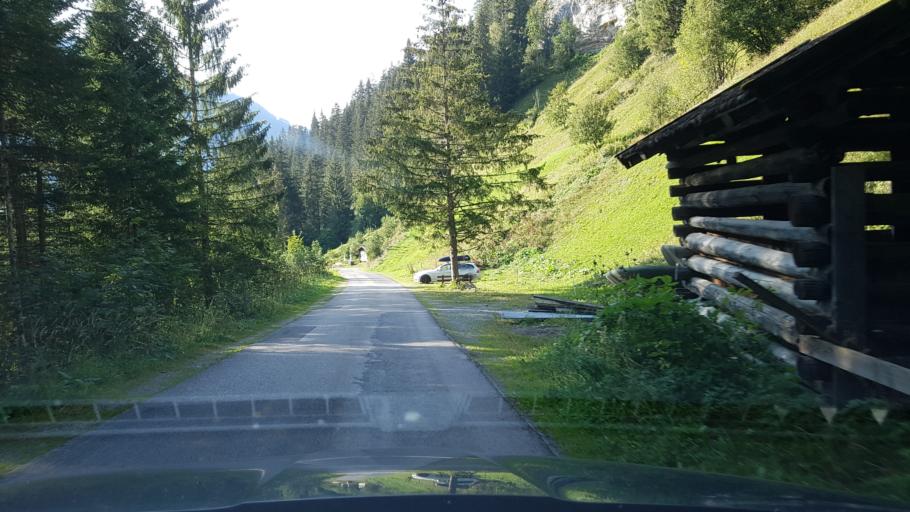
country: AT
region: Salzburg
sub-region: Politischer Bezirk Sankt Johann im Pongau
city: Kleinarl
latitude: 47.2763
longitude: 13.2390
